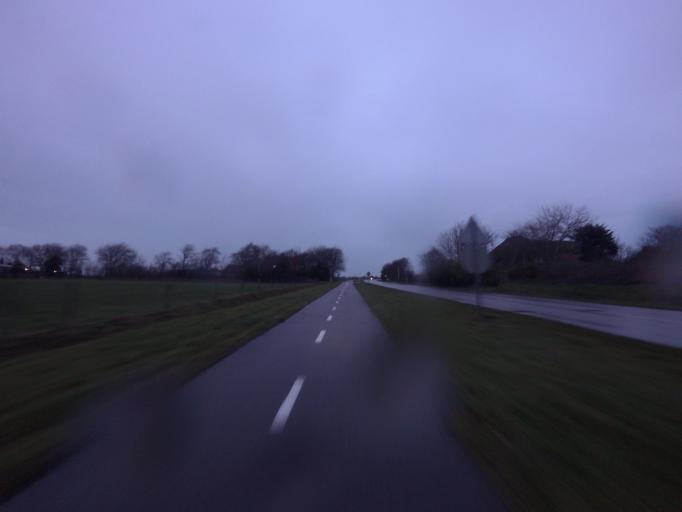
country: NL
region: North Holland
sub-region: Gemeente Texel
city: Den Burg
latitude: 53.0639
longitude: 4.8023
